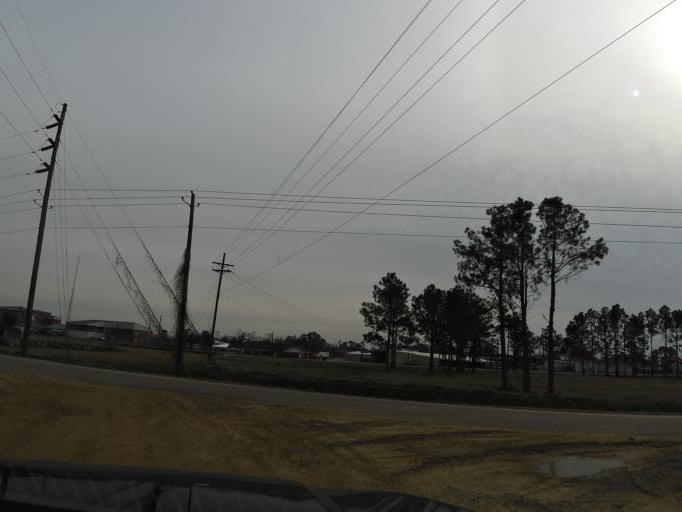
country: US
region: Georgia
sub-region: Seminole County
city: Donalsonville
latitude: 31.0436
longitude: -84.8873
